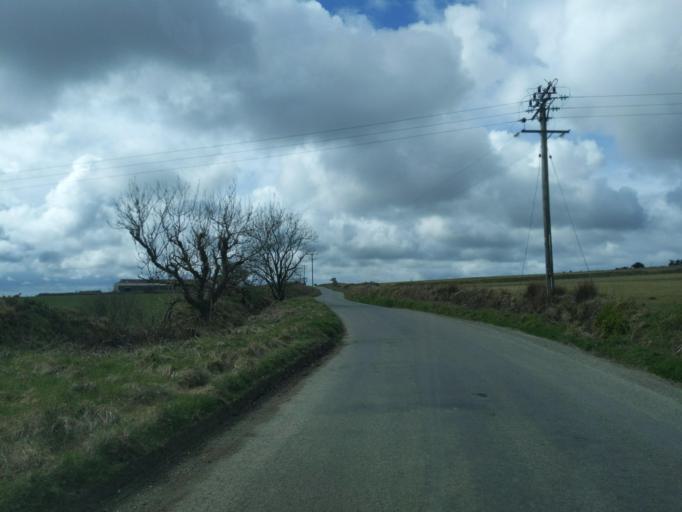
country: GB
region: England
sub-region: Cornwall
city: Camelford
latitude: 50.6408
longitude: -4.6375
